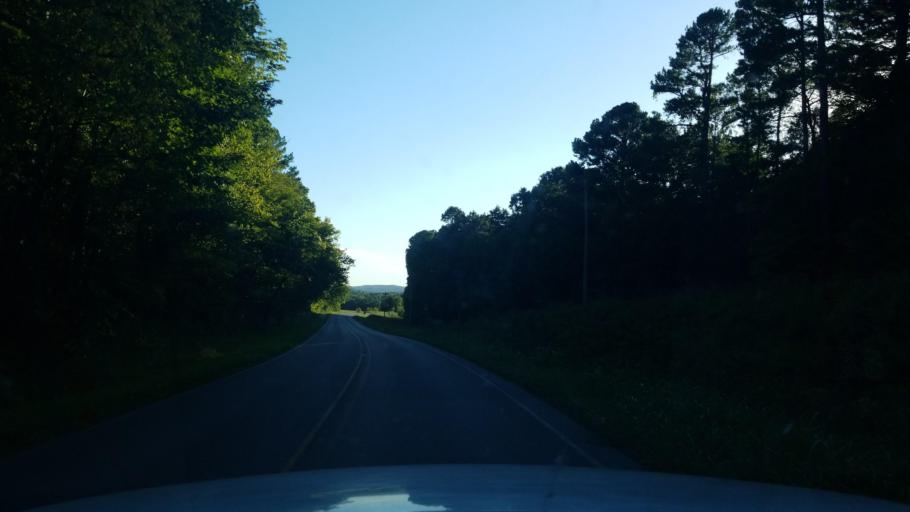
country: US
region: Illinois
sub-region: Hardin County
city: Elizabethtown
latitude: 37.5762
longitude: -88.3878
